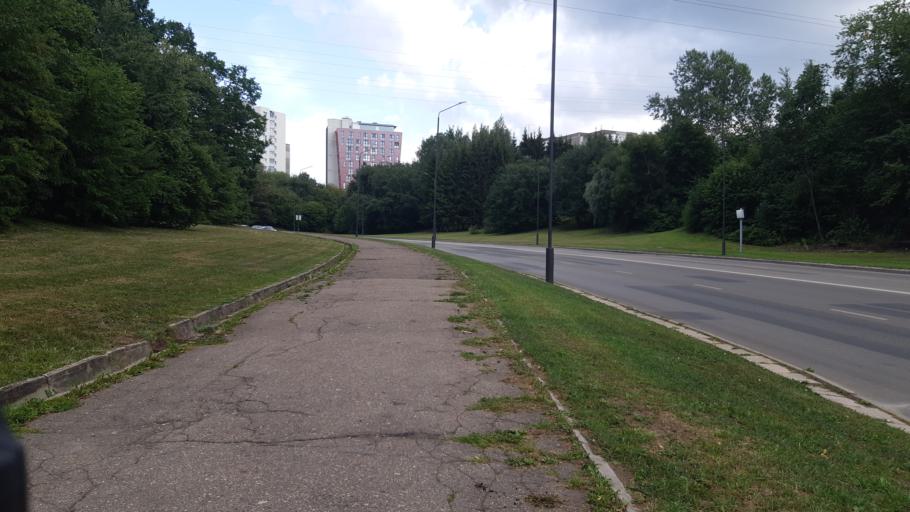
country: LT
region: Kauno apskritis
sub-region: Kaunas
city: Eiguliai
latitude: 54.9279
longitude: 23.9208
